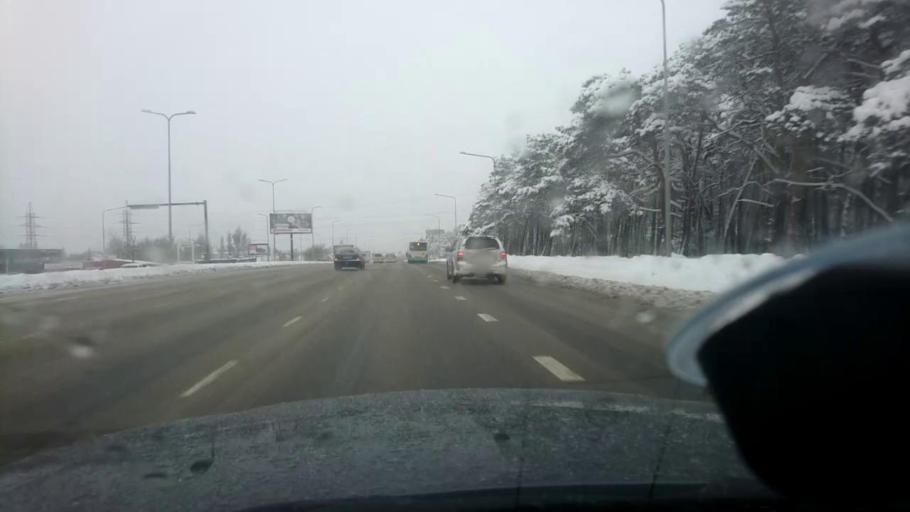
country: EE
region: Harju
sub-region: Tallinna linn
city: Tallinn
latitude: 59.3945
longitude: 24.7251
